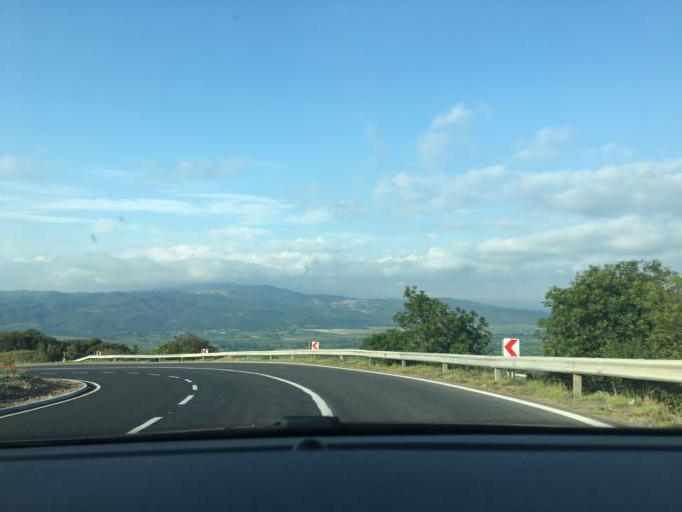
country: MK
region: Valandovo
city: Valandovo
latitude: 41.3251
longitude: 22.5962
